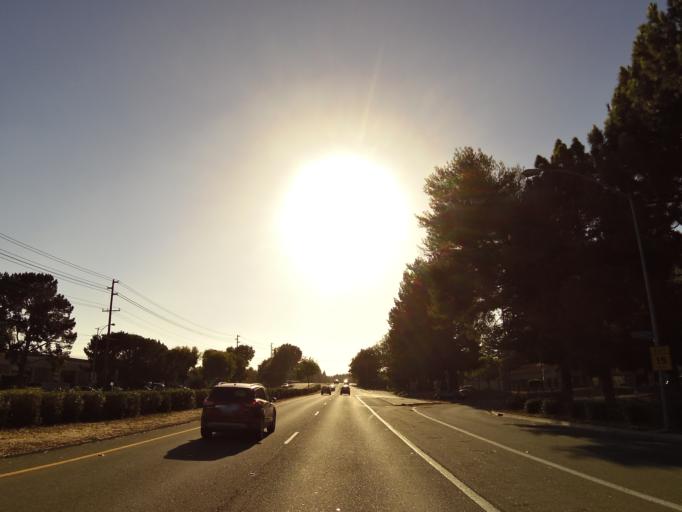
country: US
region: California
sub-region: Santa Clara County
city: Sunnyvale
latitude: 37.3778
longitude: -121.9933
